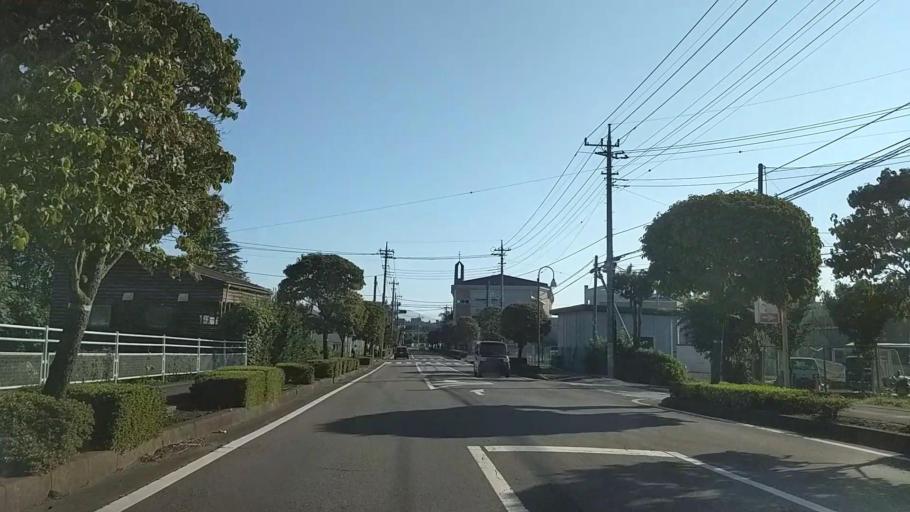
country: JP
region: Gunma
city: Annaka
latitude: 36.3253
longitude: 138.8989
